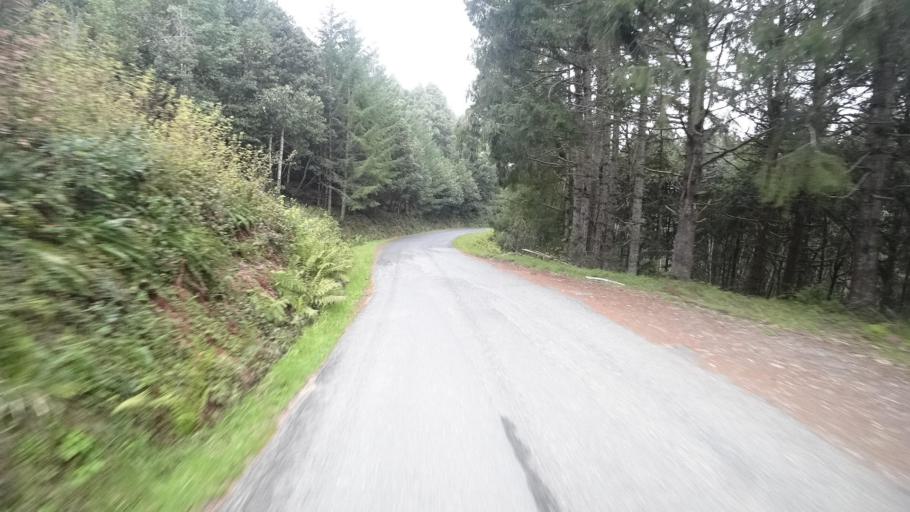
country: US
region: California
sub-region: Humboldt County
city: Redway
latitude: 40.2732
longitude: -123.7693
